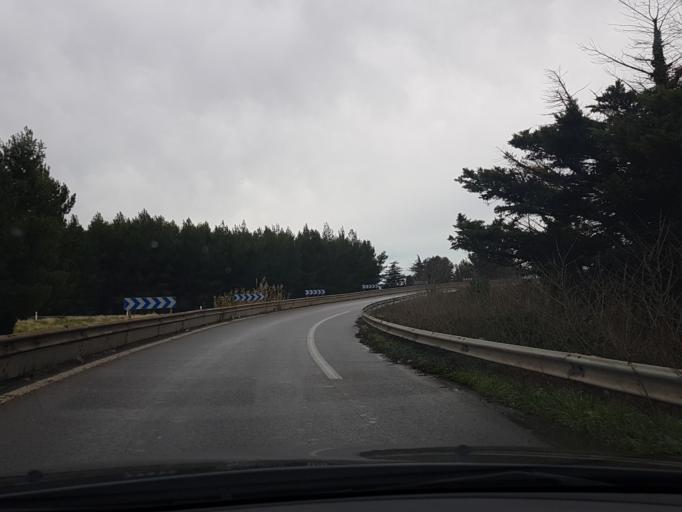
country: FR
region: Languedoc-Roussillon
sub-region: Departement du Gard
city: Nimes
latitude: 43.8123
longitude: 4.3441
